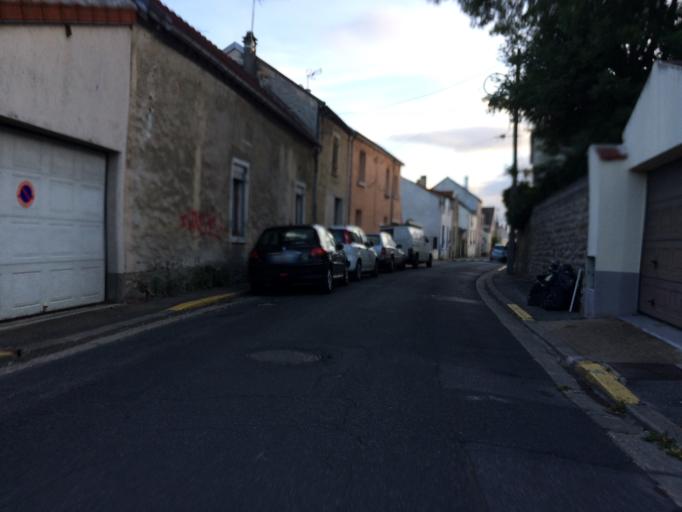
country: FR
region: Ile-de-France
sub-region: Departement de l'Essonne
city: Draveil
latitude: 48.6862
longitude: 2.4316
